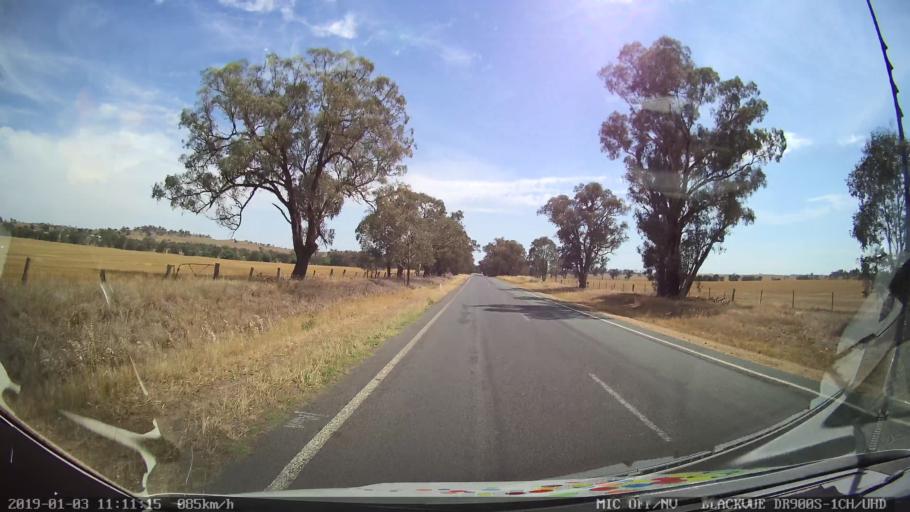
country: AU
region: New South Wales
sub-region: Young
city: Young
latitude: -34.2170
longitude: 148.2595
